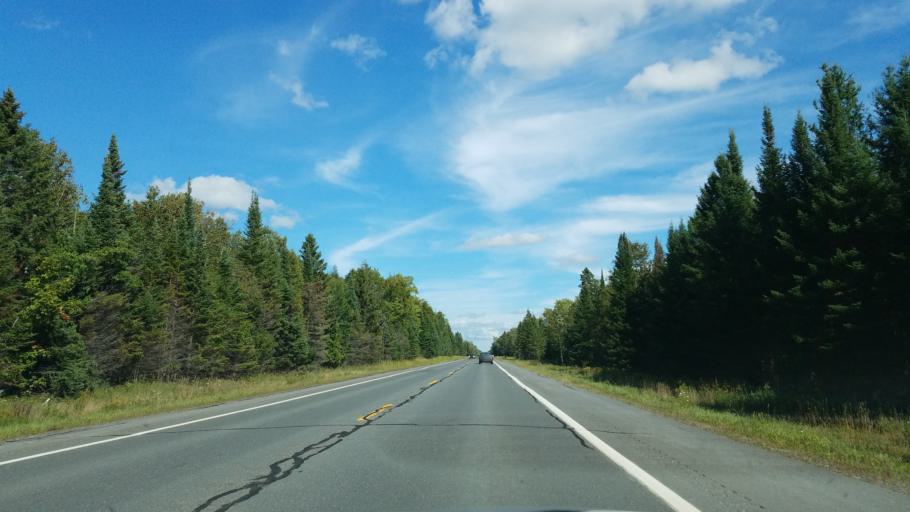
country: US
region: Michigan
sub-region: Baraga County
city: L'Anse
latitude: 46.5788
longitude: -88.4343
